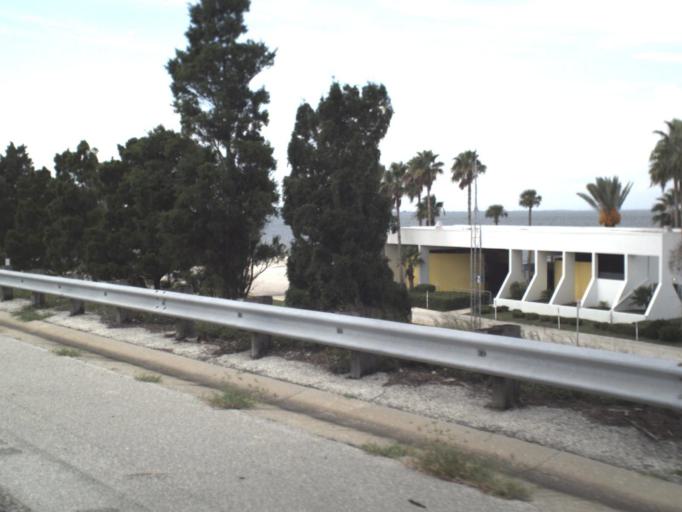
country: US
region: Florida
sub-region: Manatee County
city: Memphis
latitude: 27.5841
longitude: -82.6137
